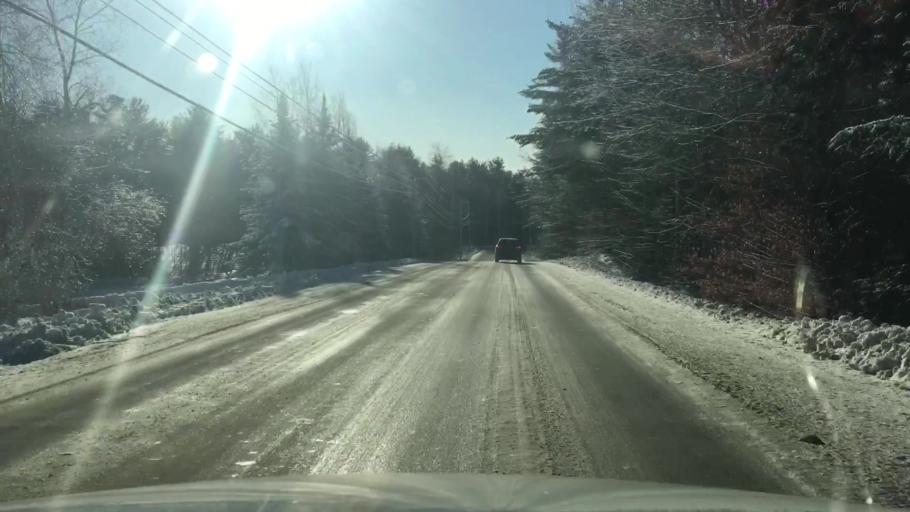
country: US
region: Maine
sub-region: Kennebec County
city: Readfield
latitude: 44.4044
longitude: -69.9642
